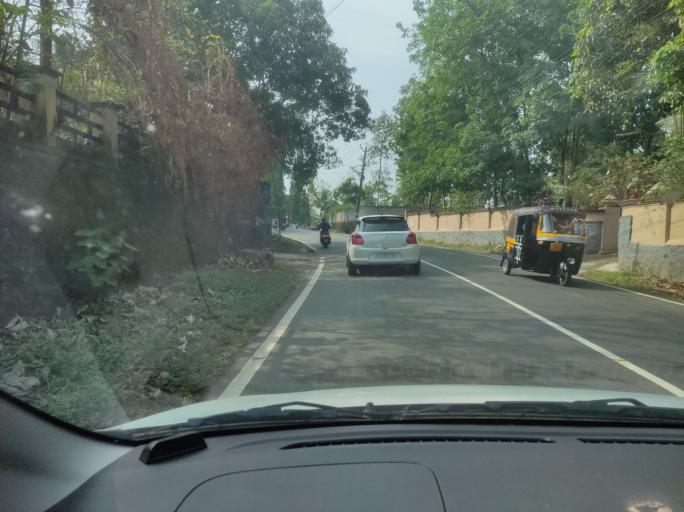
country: IN
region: Kerala
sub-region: Pattanamtitta
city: Adur
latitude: 9.1427
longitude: 76.7317
